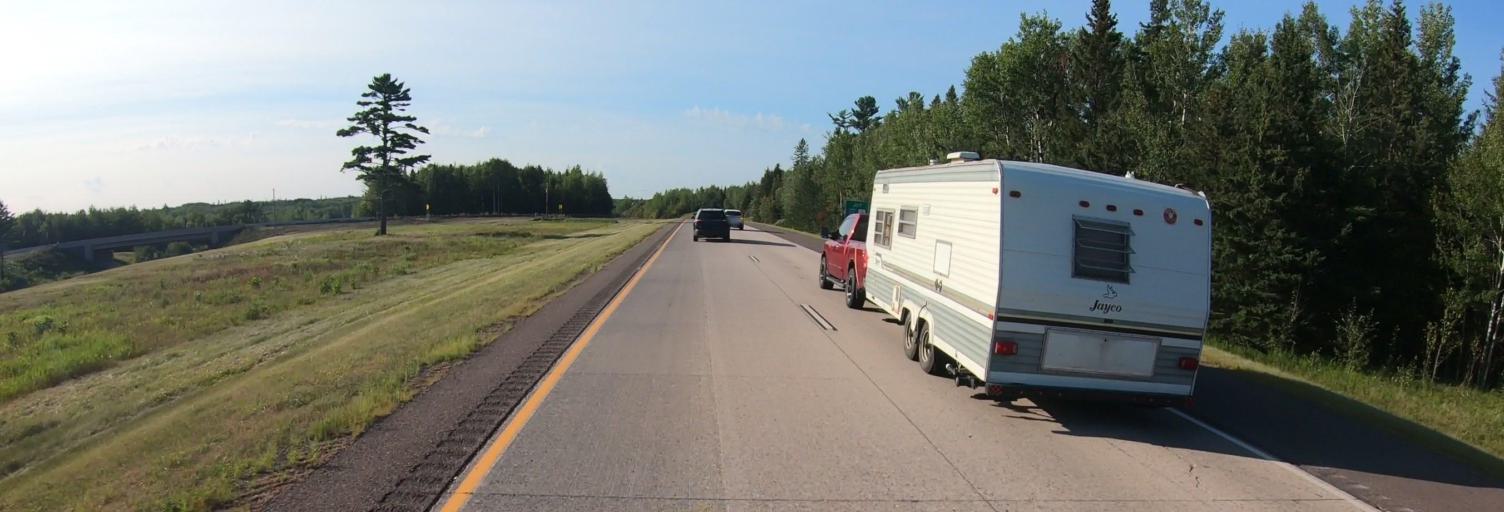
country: US
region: Minnesota
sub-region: Carlton County
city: Cloquet
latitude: 46.9541
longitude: -92.4539
